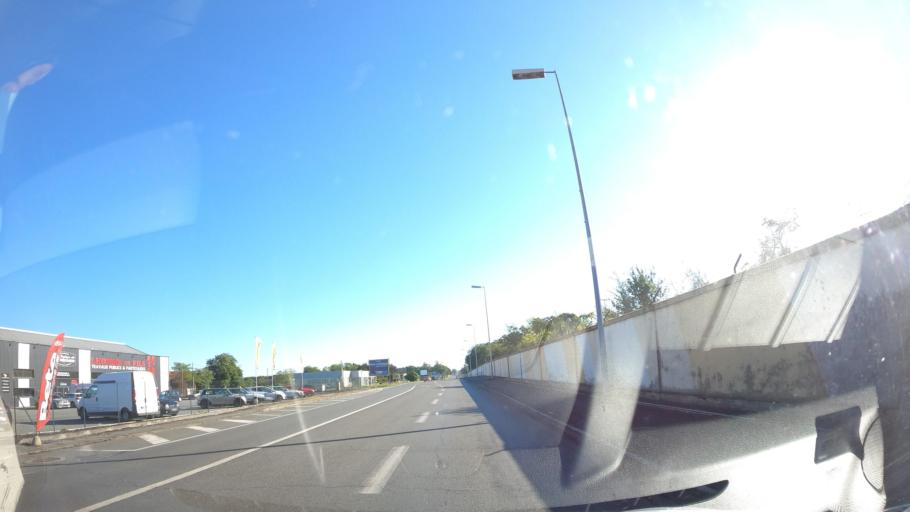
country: FR
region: Aquitaine
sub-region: Departement de la Dordogne
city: Bergerac
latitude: 44.8438
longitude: 0.5020
